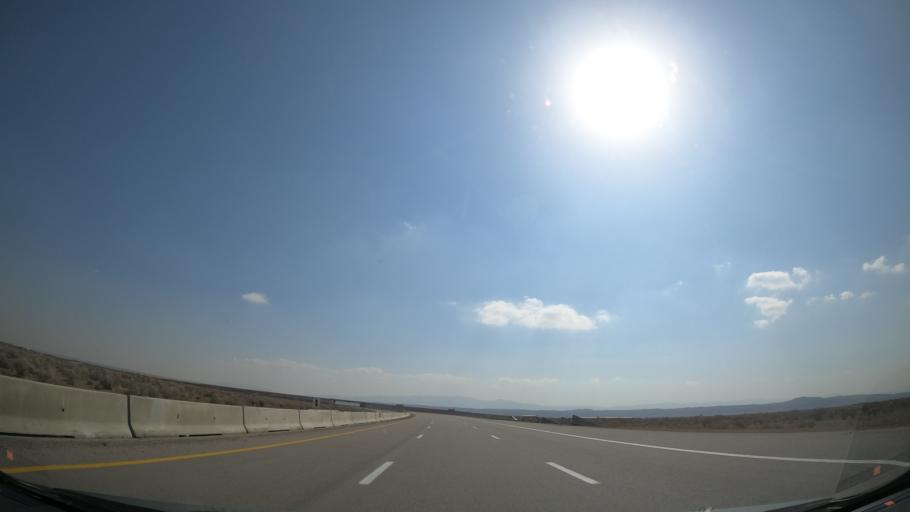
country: IR
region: Alborz
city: Nazarabad
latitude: 35.8479
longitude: 50.4813
